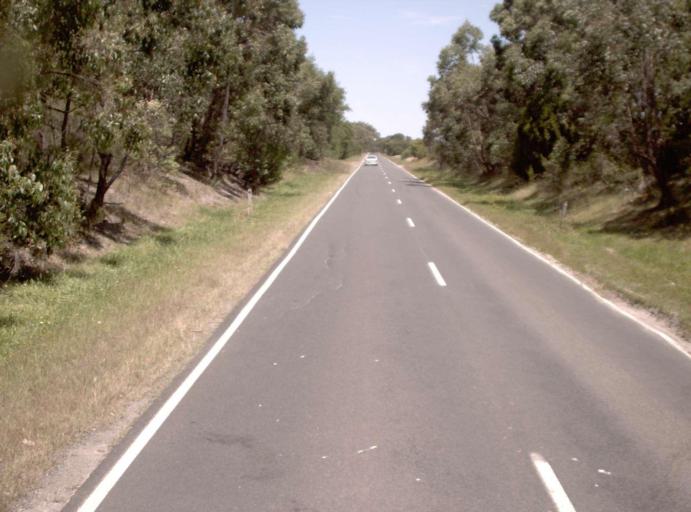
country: AU
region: Victoria
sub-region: Bass Coast
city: North Wonthaggi
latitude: -38.6723
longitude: 145.9127
